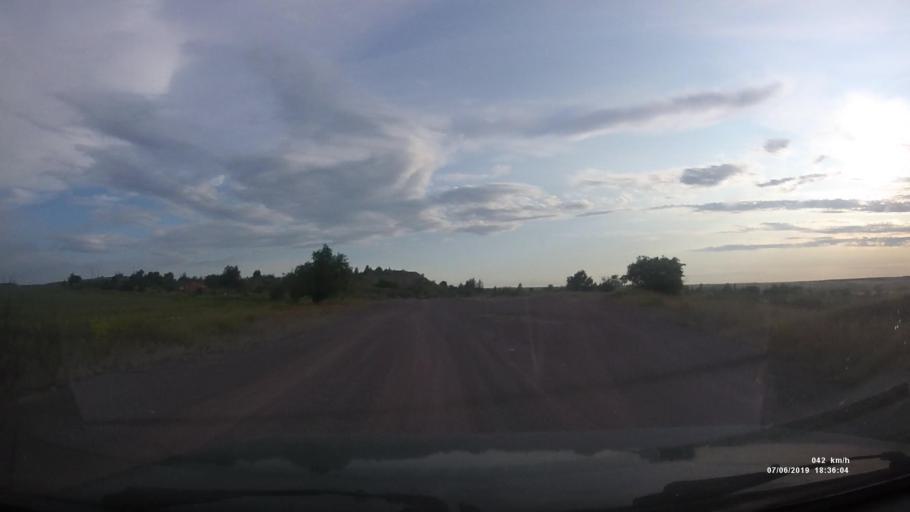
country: RU
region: Rostov
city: Staraya Stanitsa
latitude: 48.2536
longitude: 40.3553
